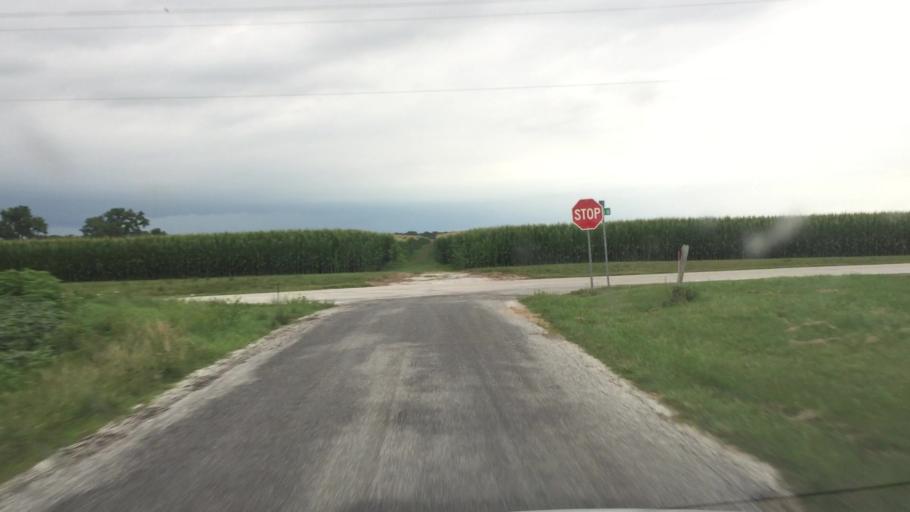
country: US
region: Illinois
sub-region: Adams County
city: Camp Point
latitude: 40.2301
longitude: -90.9690
